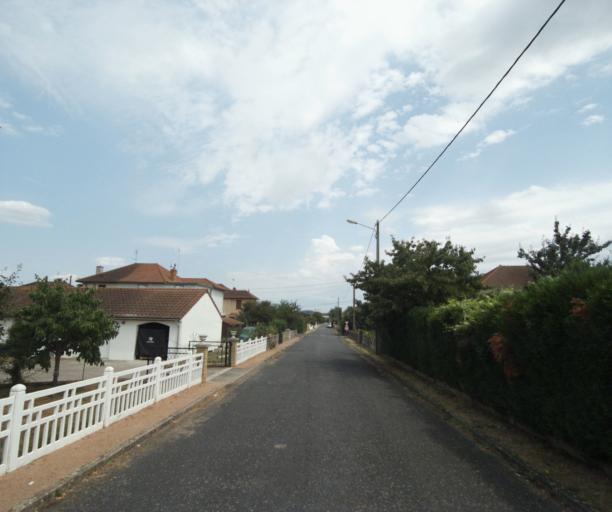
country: FR
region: Bourgogne
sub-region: Departement de Saone-et-Loire
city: Gueugnon
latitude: 46.6081
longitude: 4.0517
